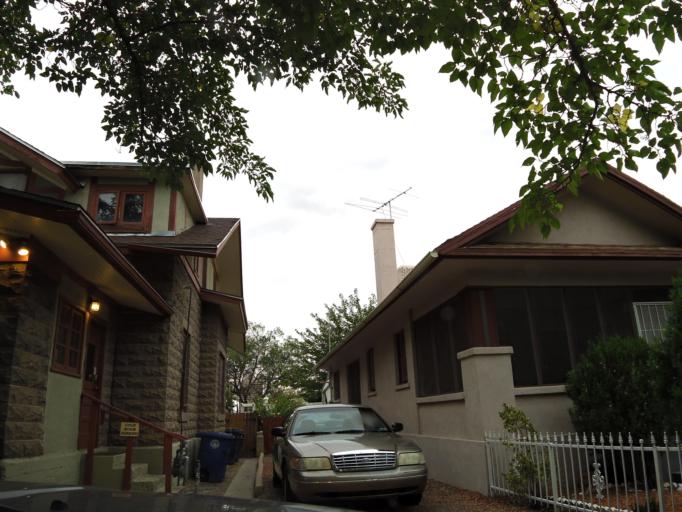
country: US
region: New Mexico
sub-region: Bernalillo County
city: Albuquerque
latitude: 35.0845
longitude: -106.6396
